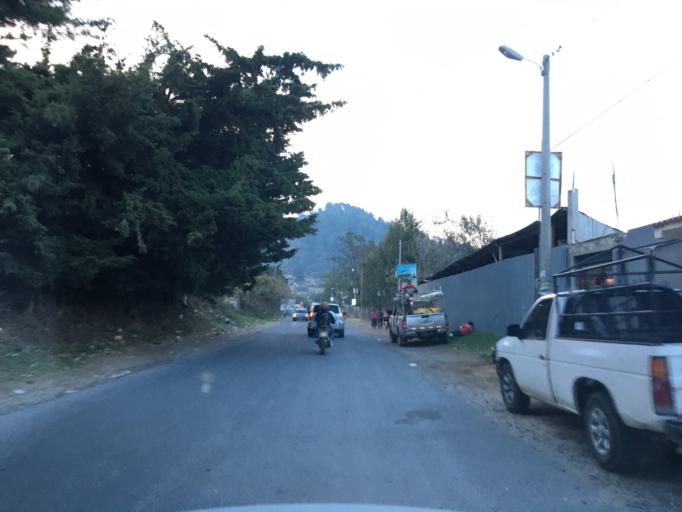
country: GT
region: Chimaltenango
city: Tecpan Guatemala
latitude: 14.7546
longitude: -90.9995
